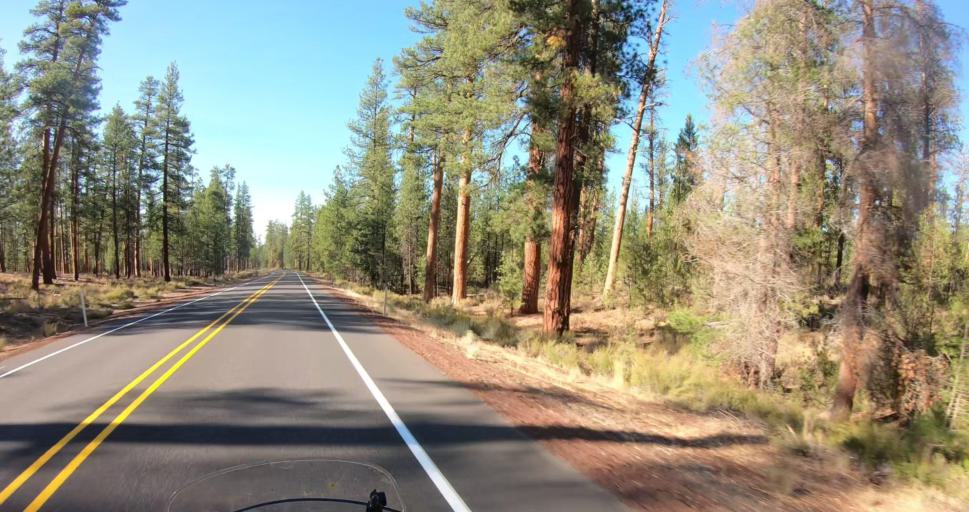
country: US
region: Oregon
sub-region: Deschutes County
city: La Pine
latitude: 43.4709
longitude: -121.3999
